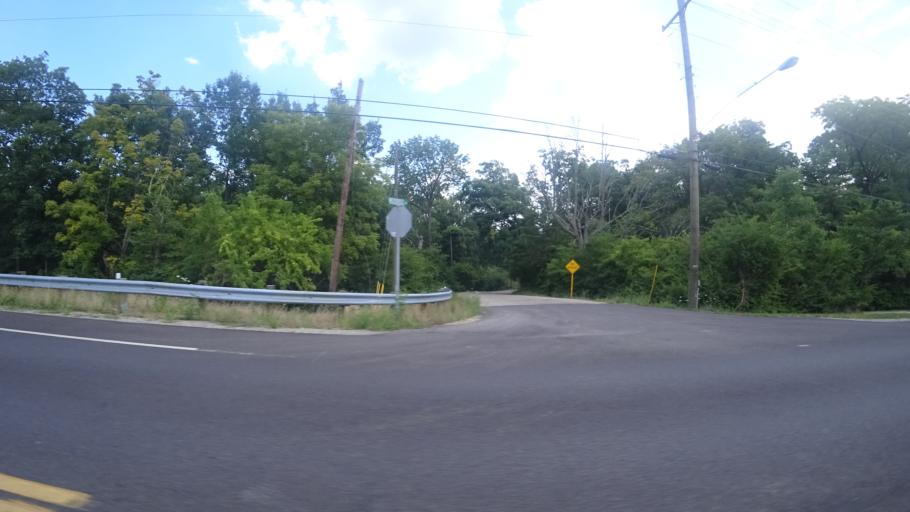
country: US
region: Ohio
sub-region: Butler County
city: Hamilton
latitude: 39.4371
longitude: -84.6068
